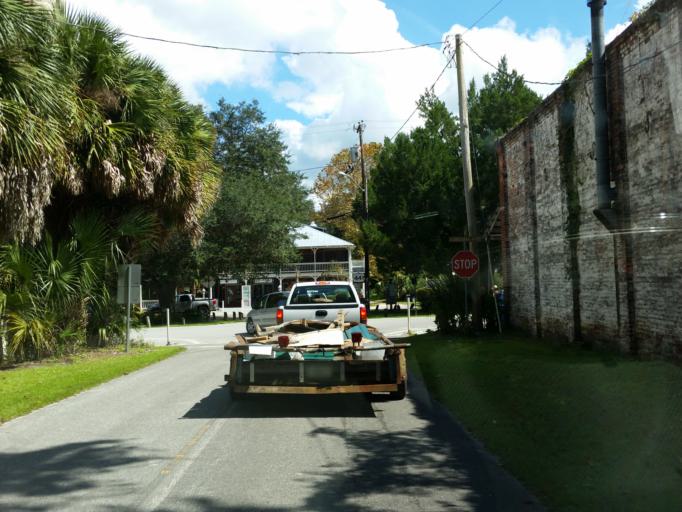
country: US
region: Florida
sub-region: Alachua County
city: Gainesville
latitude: 29.5045
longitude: -82.2800
